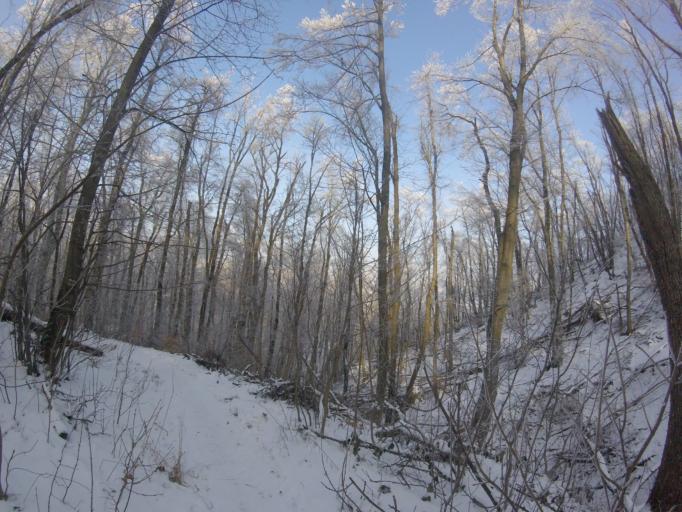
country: HU
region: Pest
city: Pilisszentivan
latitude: 47.5954
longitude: 18.8716
